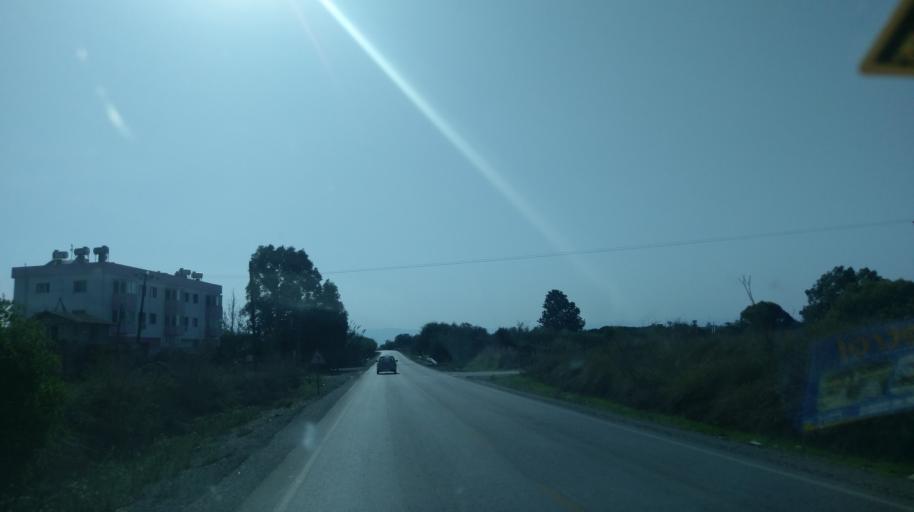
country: CY
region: Lefkosia
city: Morfou
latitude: 35.2184
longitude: 33.0064
